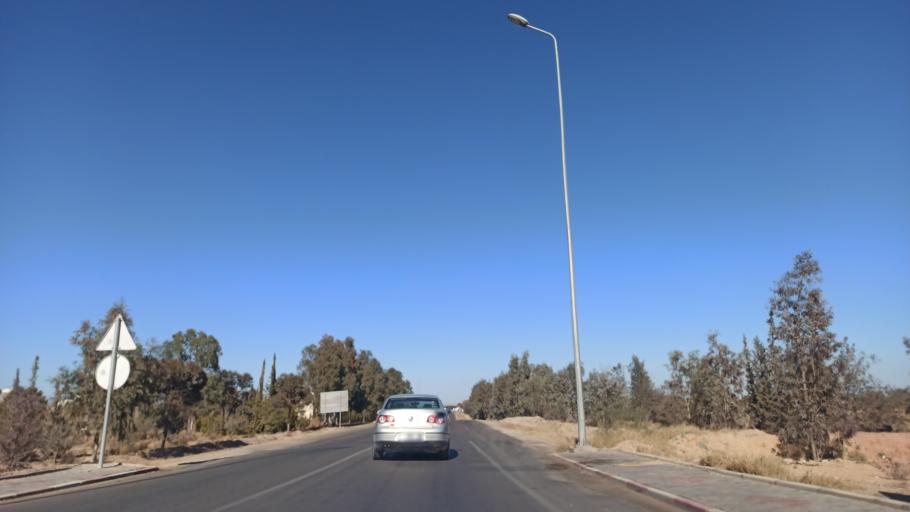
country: TN
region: Sidi Bu Zayd
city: Jilma
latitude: 35.1395
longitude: 9.3612
